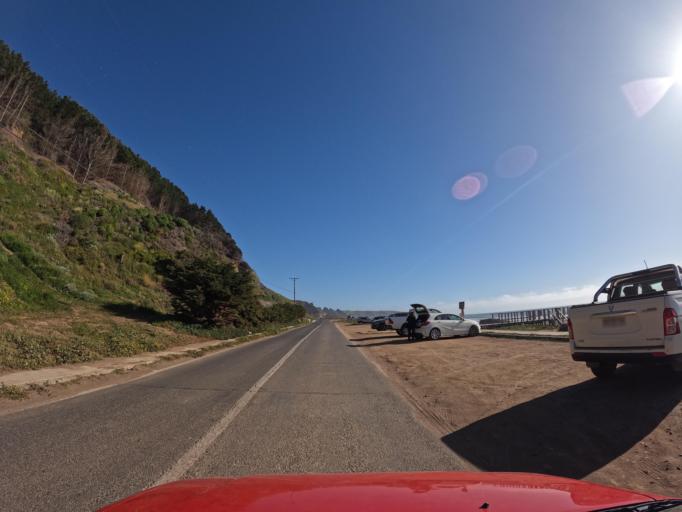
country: CL
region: Maule
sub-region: Provincia de Talca
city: Constitucion
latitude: -34.8609
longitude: -72.1469
